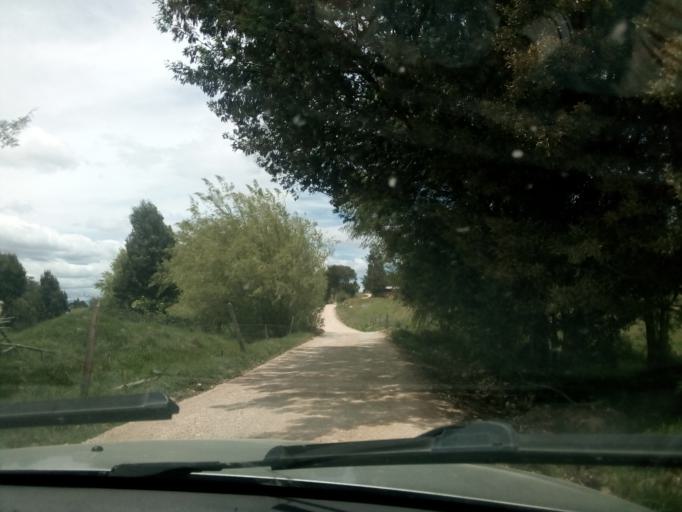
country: CO
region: Boyaca
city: Toca
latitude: 5.5975
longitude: -73.1580
